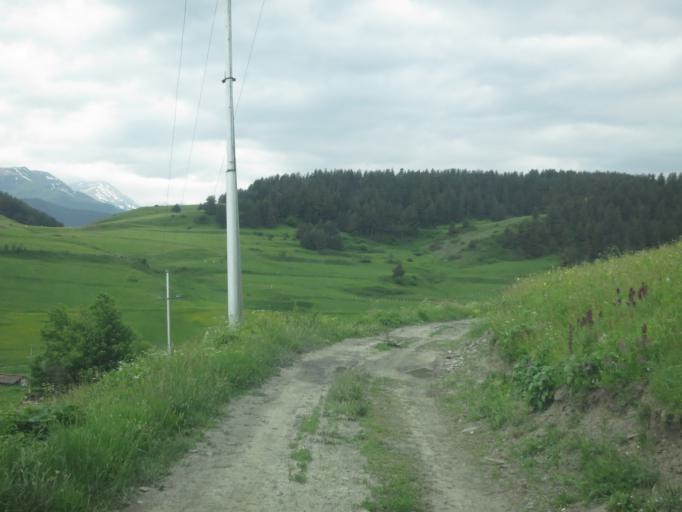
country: RU
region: Chechnya
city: Itum-Kali
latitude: 42.3752
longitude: 45.6617
